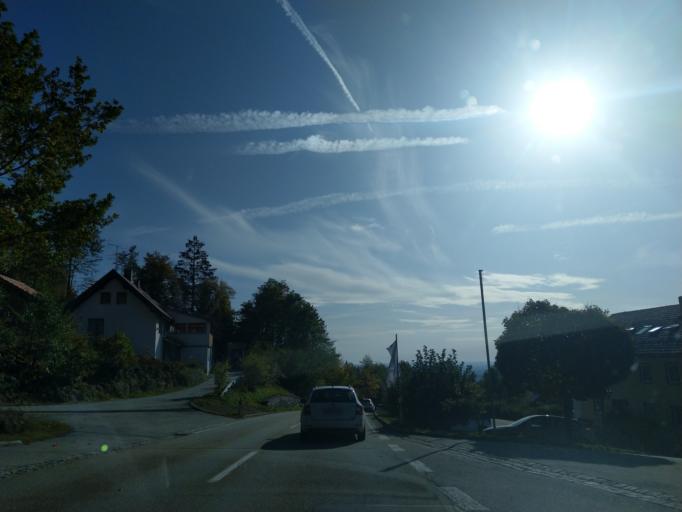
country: DE
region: Bavaria
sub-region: Lower Bavaria
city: Achslach
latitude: 48.9302
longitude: 12.9265
